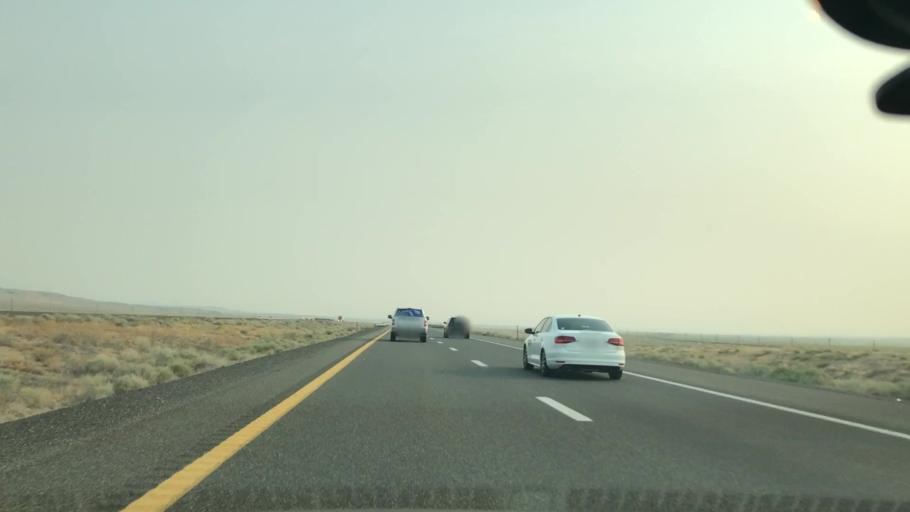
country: US
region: Nevada
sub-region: Pershing County
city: Lovelock
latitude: 40.0080
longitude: -118.6776
